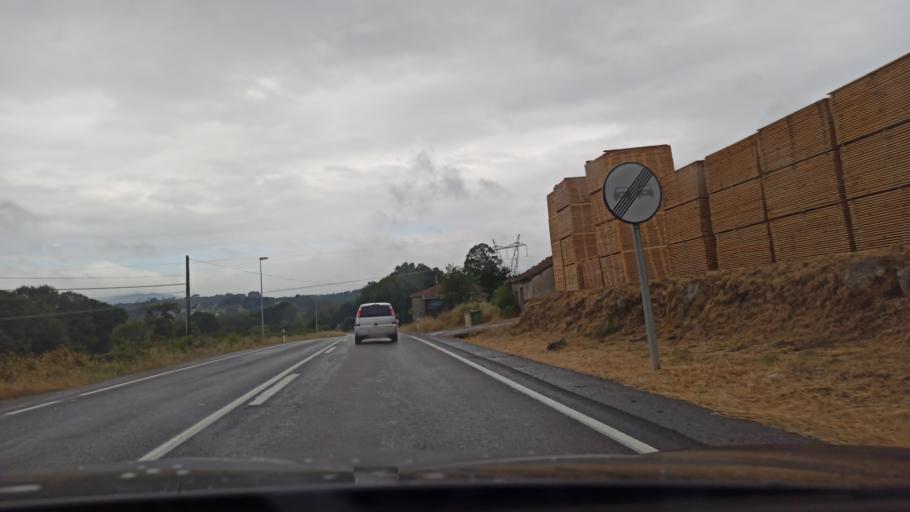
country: ES
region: Galicia
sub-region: Provincia de Lugo
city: Monterroso
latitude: 42.7925
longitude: -7.8469
